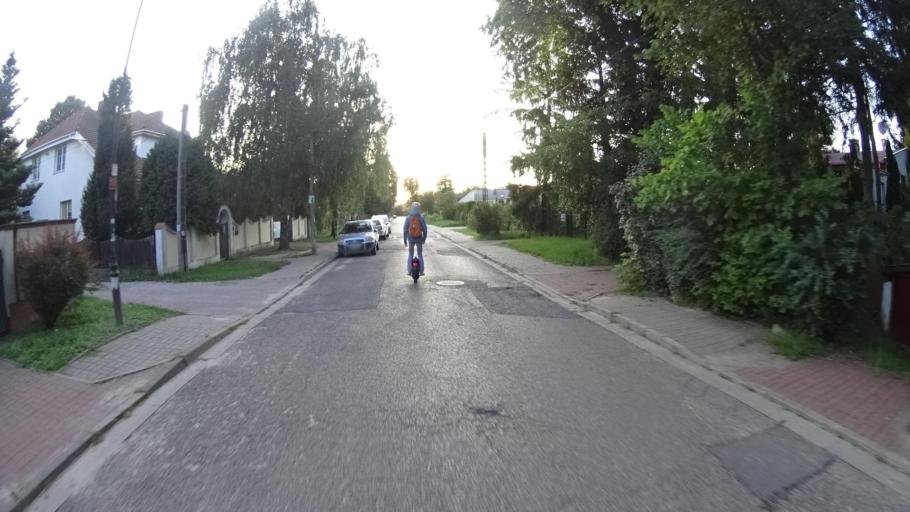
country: PL
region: Masovian Voivodeship
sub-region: Warszawa
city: Bielany
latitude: 52.3058
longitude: 20.9391
